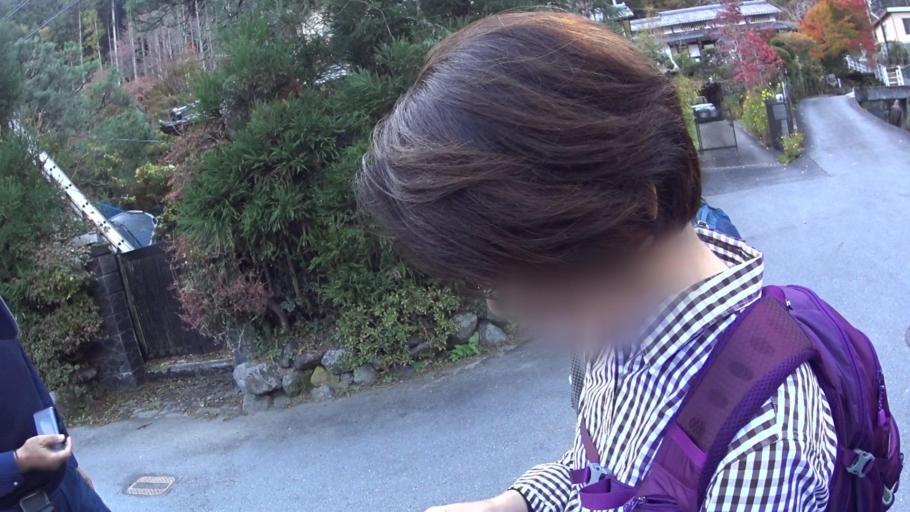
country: JP
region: Kyoto
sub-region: Kyoto-shi
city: Kamigyo-ku
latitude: 35.0994
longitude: 135.7624
